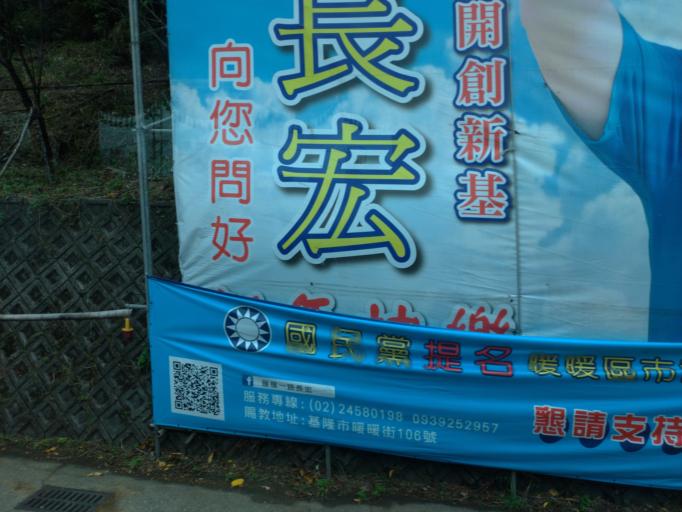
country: TW
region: Taiwan
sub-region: Keelung
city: Keelung
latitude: 25.0997
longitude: 121.7465
